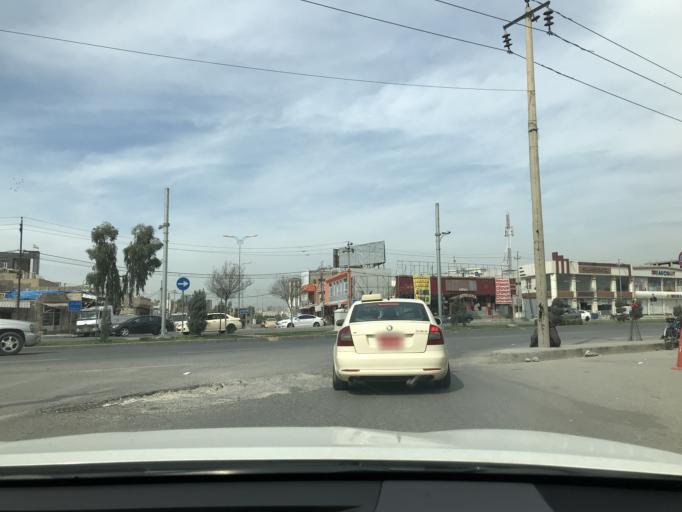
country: IQ
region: Arbil
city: Erbil
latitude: 36.1731
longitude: 44.0381
